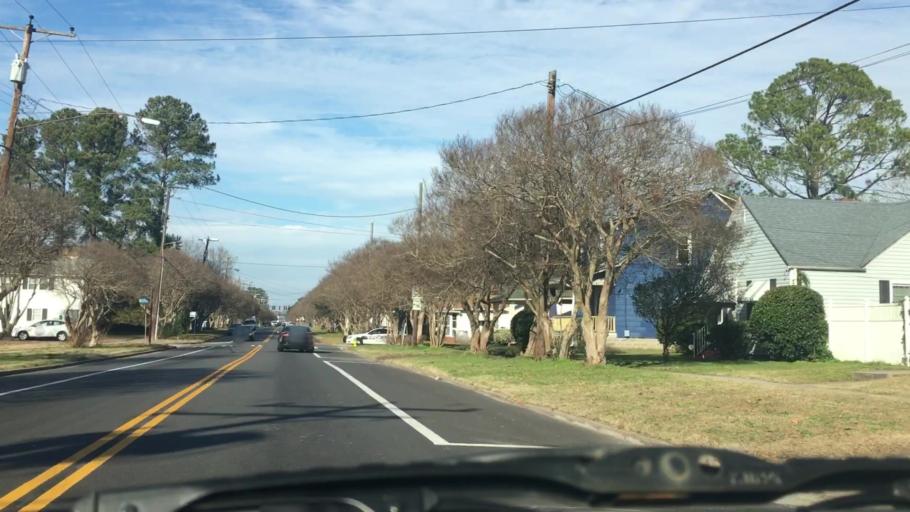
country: US
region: Virginia
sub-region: City of Norfolk
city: Norfolk
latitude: 36.8653
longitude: -76.2510
